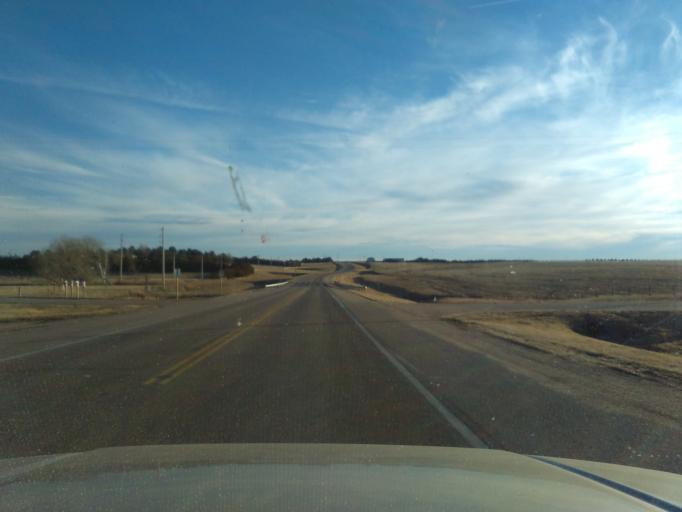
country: US
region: Kansas
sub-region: Logan County
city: Oakley
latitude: 39.1852
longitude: -100.8699
